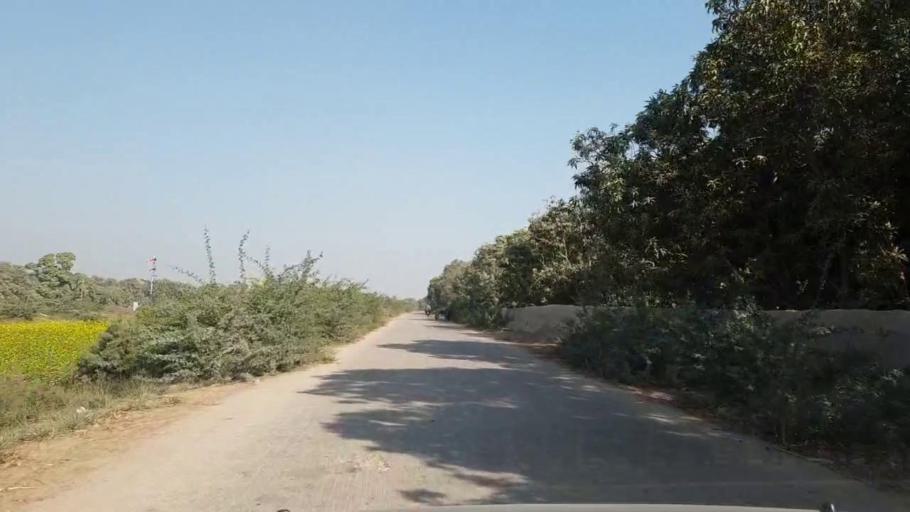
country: PK
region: Sindh
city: Matiari
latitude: 25.6212
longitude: 68.5914
